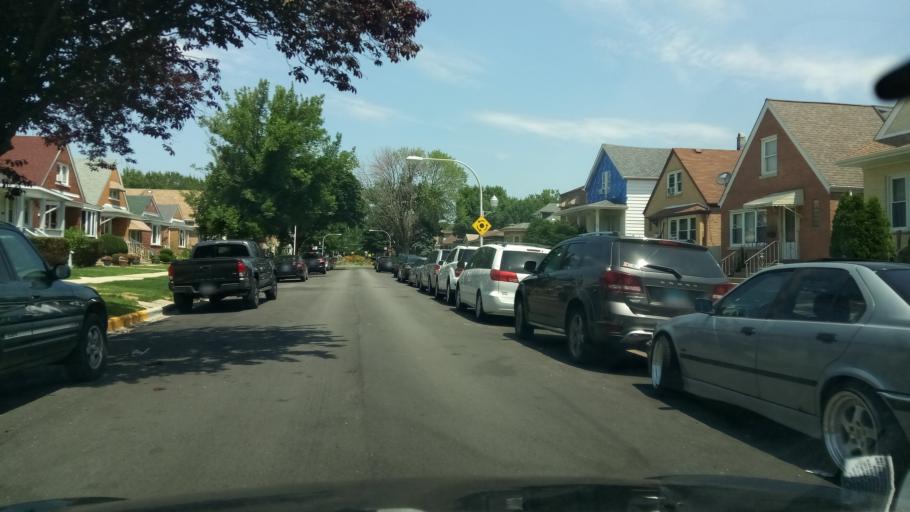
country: US
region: Illinois
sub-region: Cook County
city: Hometown
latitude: 41.7829
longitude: -87.7314
